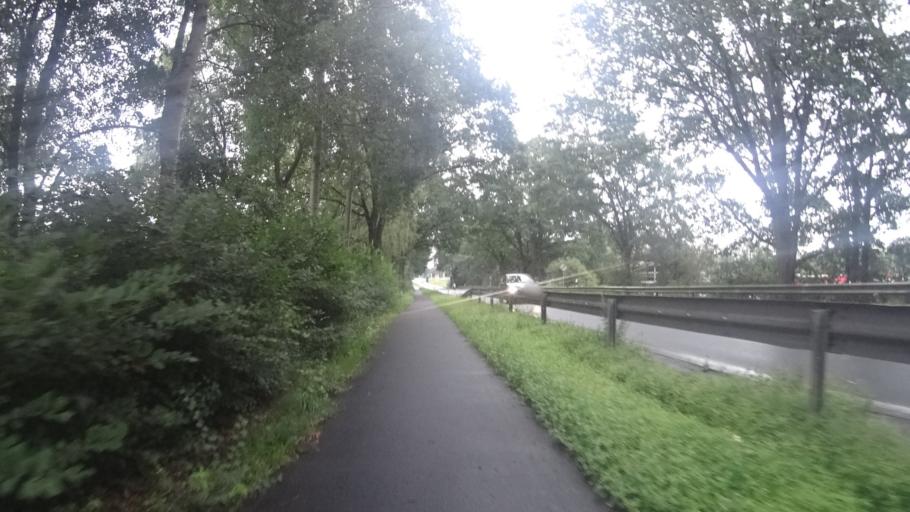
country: DE
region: Schleswig-Holstein
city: Elmshorn
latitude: 53.7779
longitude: 9.6540
